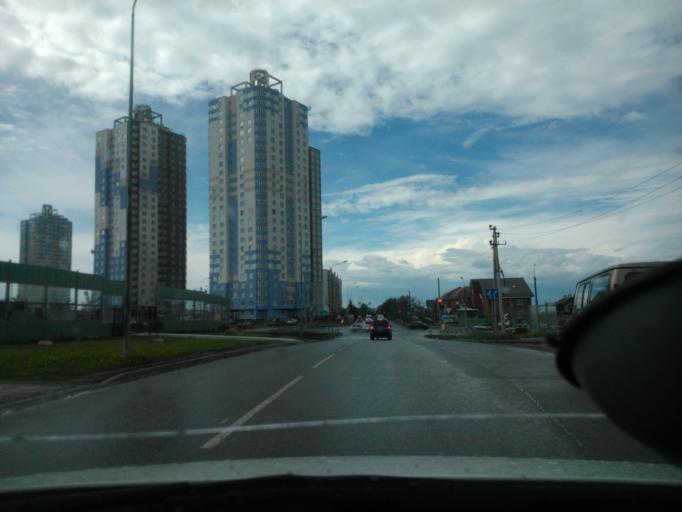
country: RU
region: Perm
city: Perm
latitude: 58.0041
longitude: 56.3286
